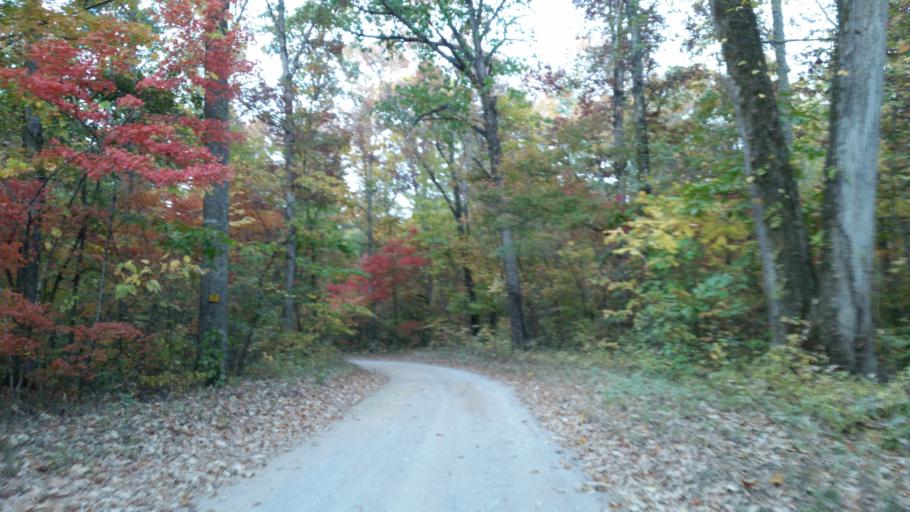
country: US
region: Georgia
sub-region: Gordon County
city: Calhoun
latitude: 34.6111
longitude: -85.0480
